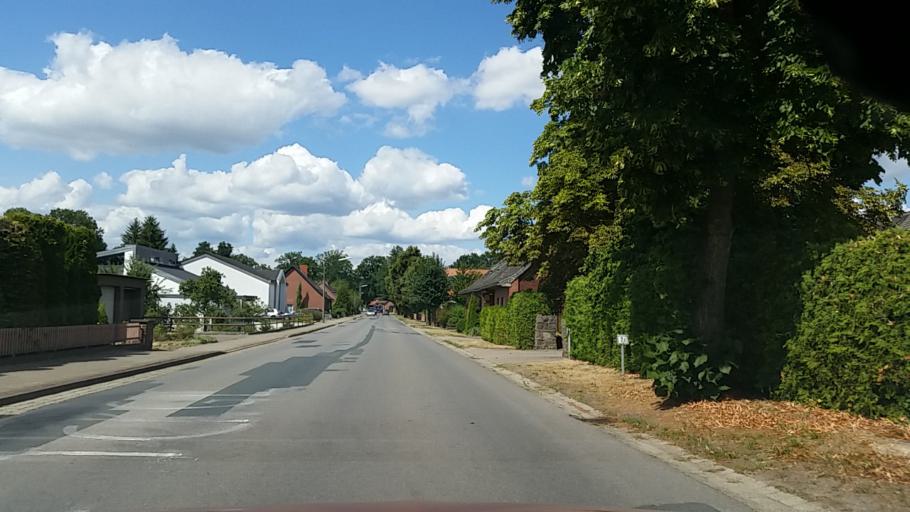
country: DE
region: Lower Saxony
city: Hankensbuttel
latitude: 52.7173
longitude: 10.6219
